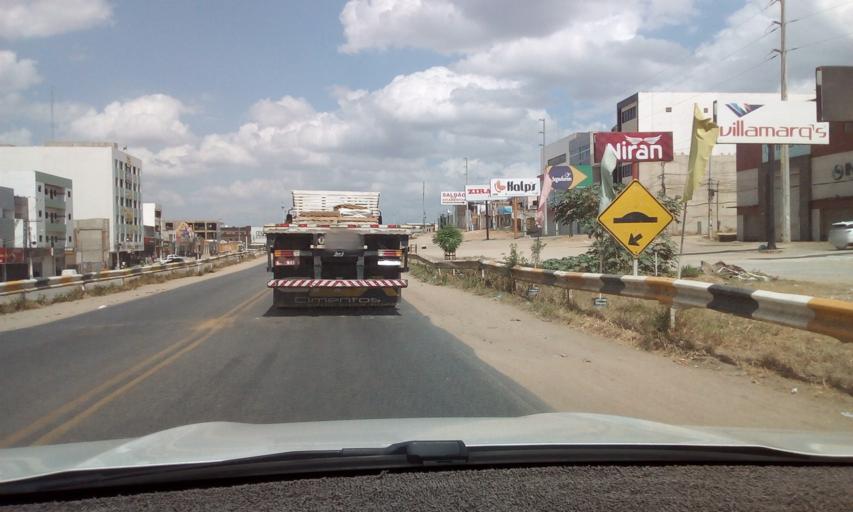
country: BR
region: Pernambuco
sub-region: Toritama
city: Toritama
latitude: -8.0075
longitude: -36.0643
